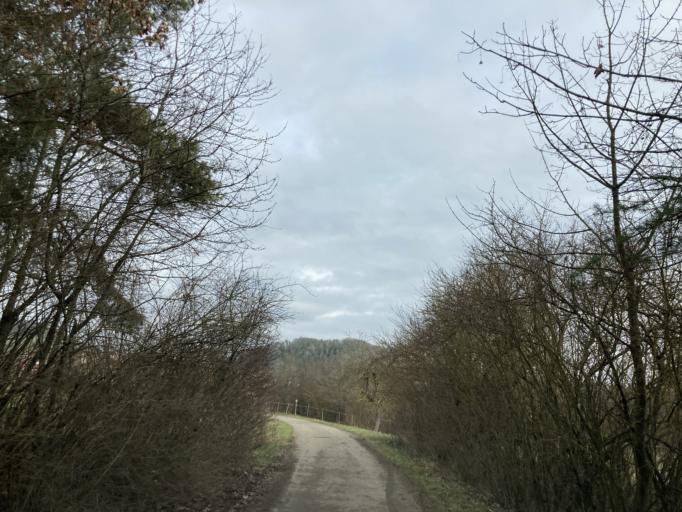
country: DE
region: Baden-Wuerttemberg
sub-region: Tuebingen Region
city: Rottenburg
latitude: 48.4472
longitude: 8.9132
